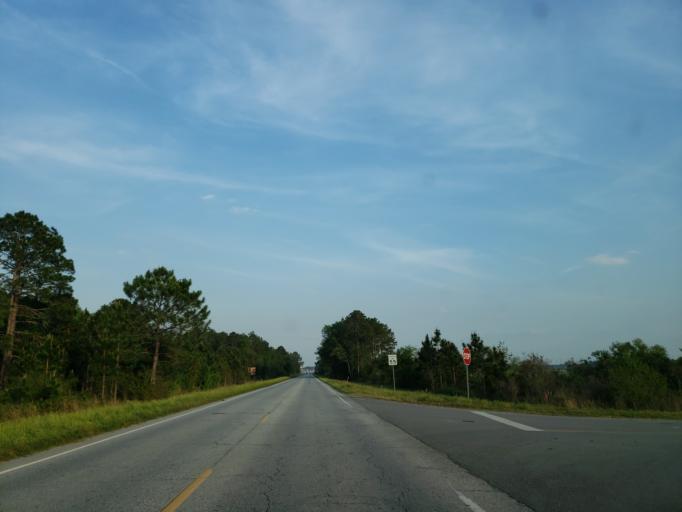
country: US
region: Georgia
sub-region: Cook County
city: Sparks
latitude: 31.1457
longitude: -83.4572
